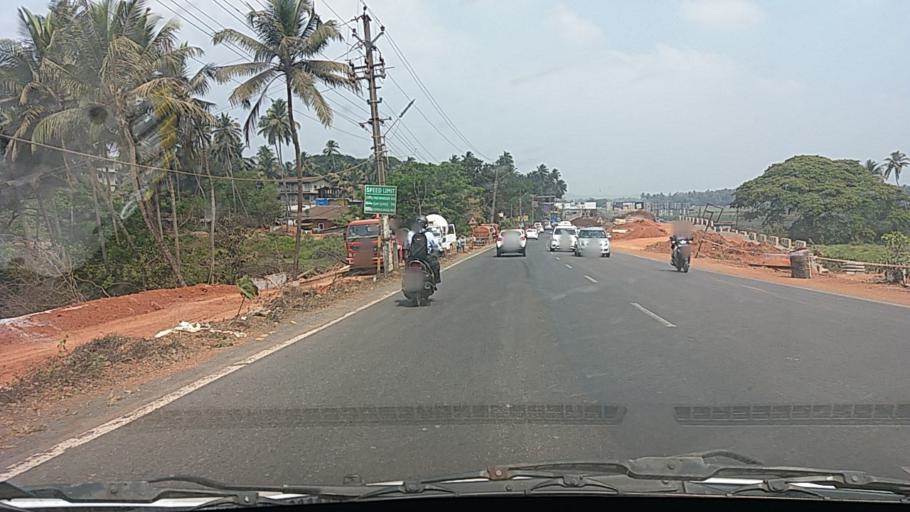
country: IN
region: Goa
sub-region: North Goa
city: Bambolim
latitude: 15.4702
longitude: 73.8506
